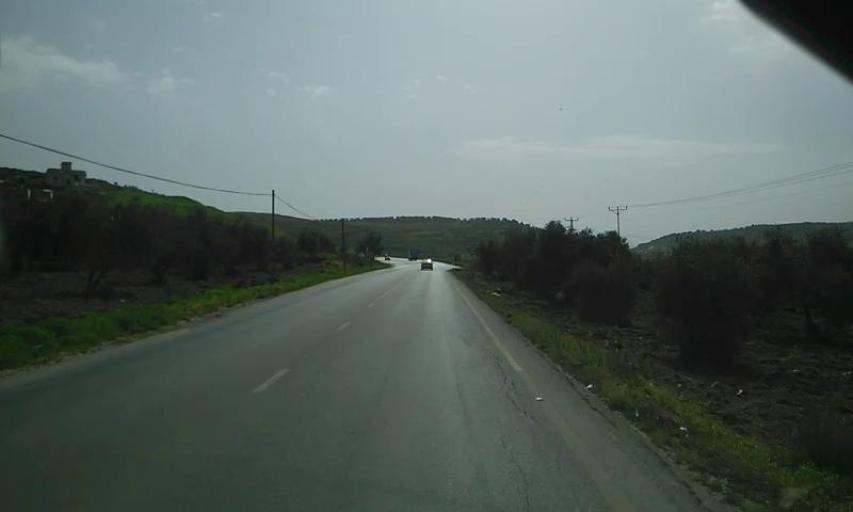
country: PS
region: West Bank
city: `Arrabah
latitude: 32.3887
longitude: 35.2163
